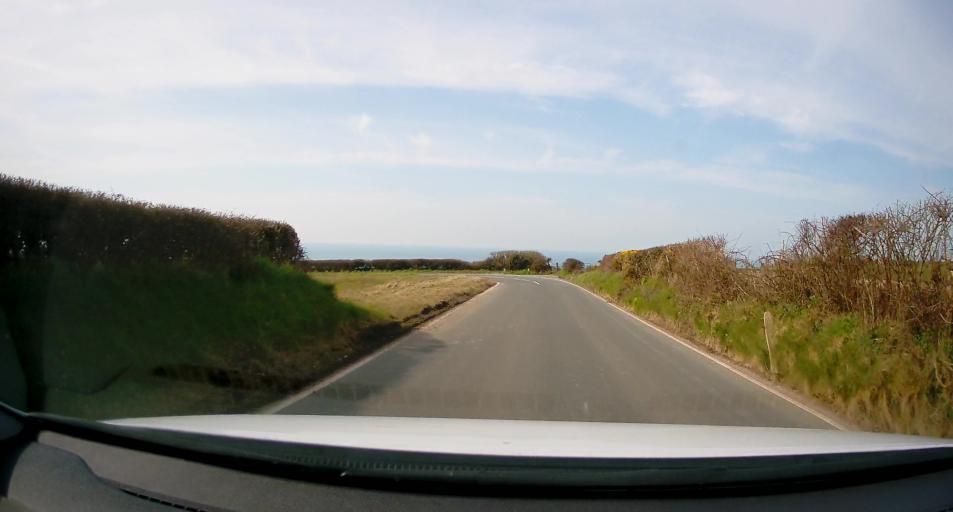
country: GB
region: Wales
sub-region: County of Ceredigion
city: Llanon
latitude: 52.2552
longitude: -4.2149
